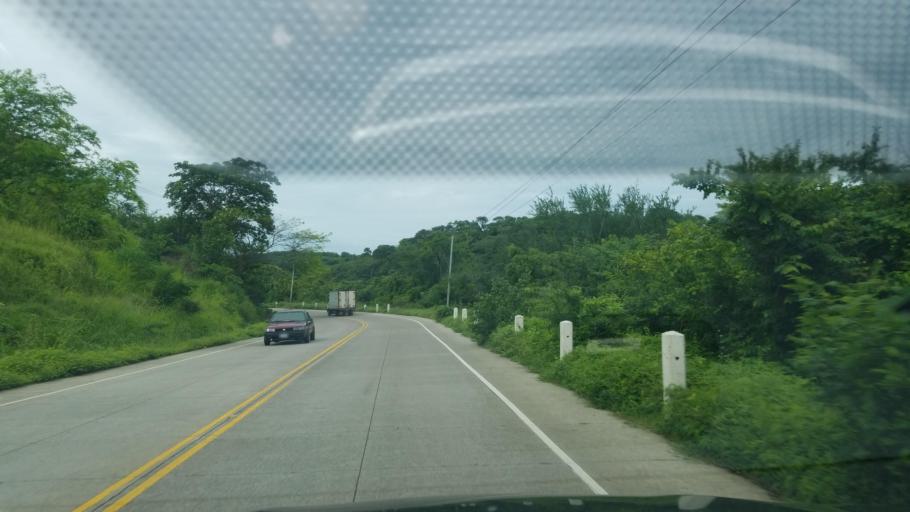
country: HN
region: Choluteca
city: Pespire
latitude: 13.6234
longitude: -87.3740
